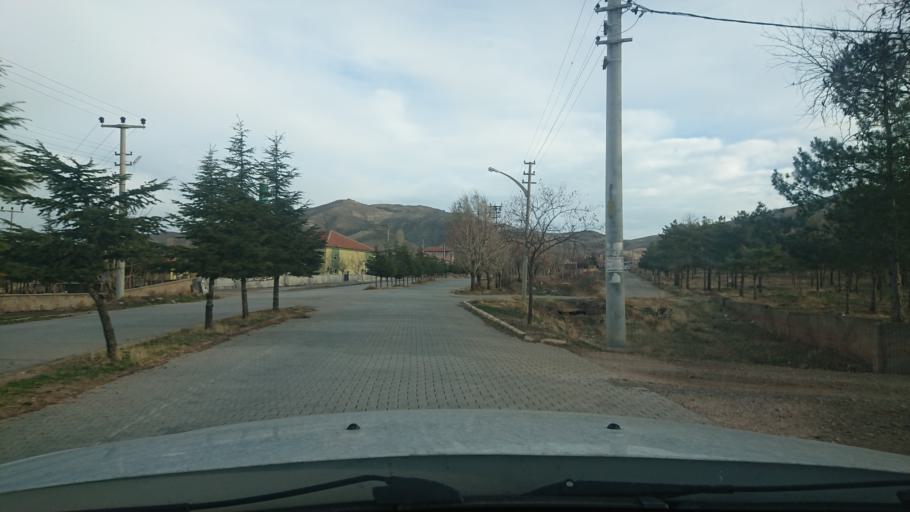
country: TR
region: Aksaray
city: Acipinar
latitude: 38.6117
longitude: 33.7790
